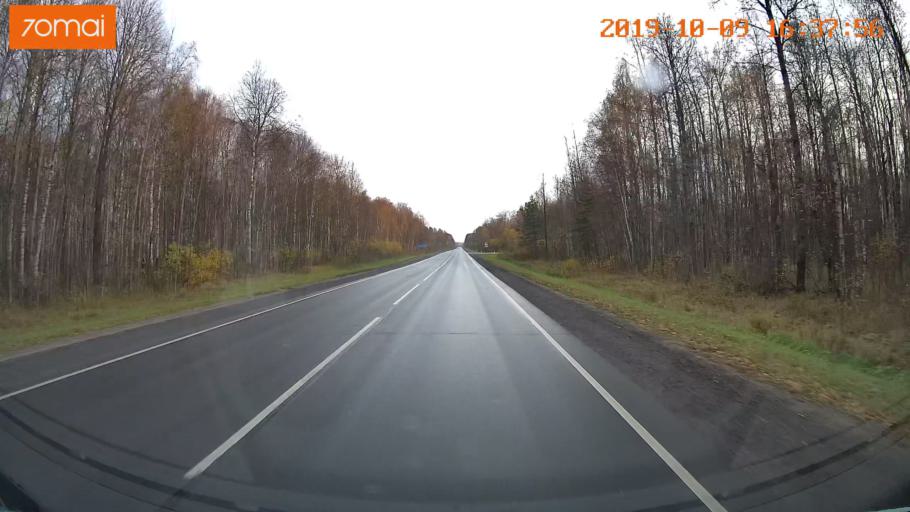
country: RU
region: Kostroma
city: Volgorechensk
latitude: 57.5196
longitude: 41.0307
